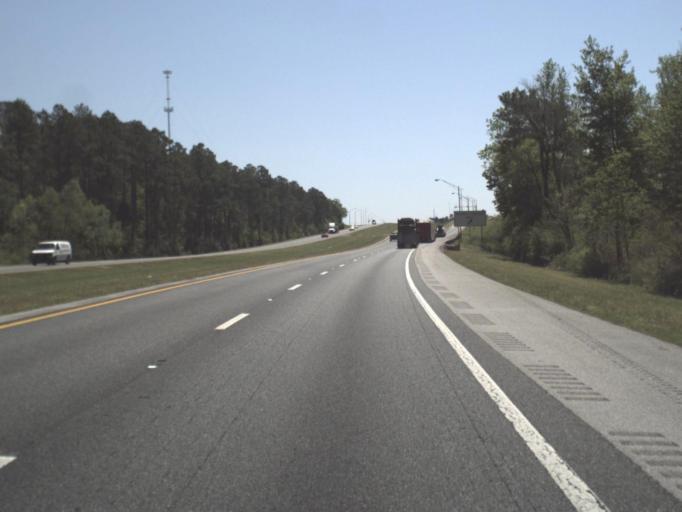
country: US
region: Florida
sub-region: Escambia County
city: Cantonment
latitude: 30.5612
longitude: -87.3740
